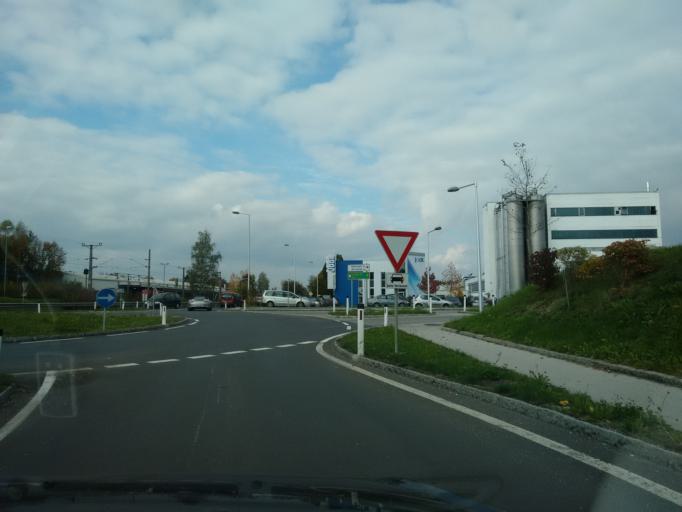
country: AT
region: Upper Austria
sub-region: Politischer Bezirk Vocklabruck
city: Lenzing
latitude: 47.9806
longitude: 13.6153
